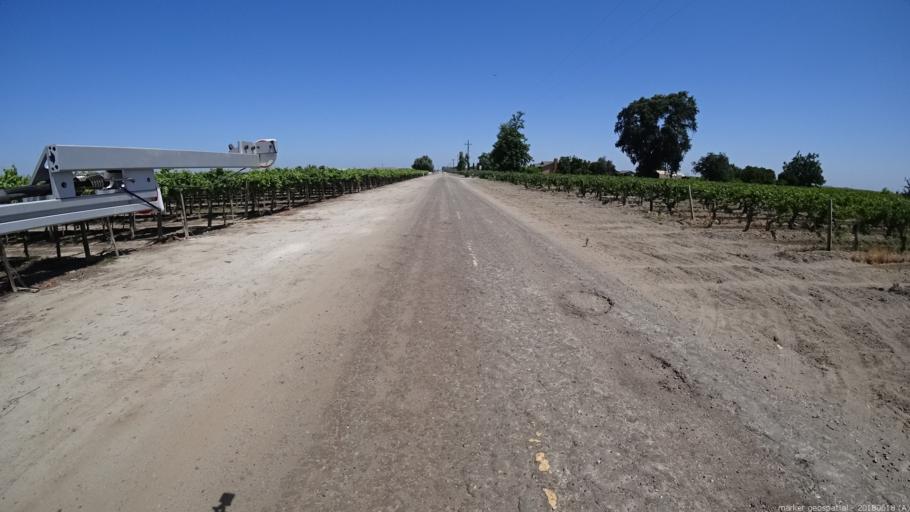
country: US
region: California
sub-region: Madera County
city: Parkwood
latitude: 36.8600
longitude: -120.1194
